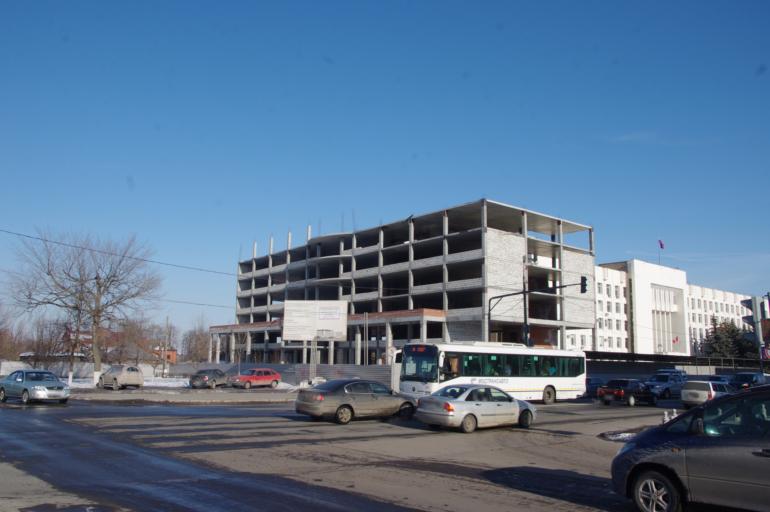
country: RU
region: Moskovskaya
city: Kolomna
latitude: 55.0964
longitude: 38.7637
